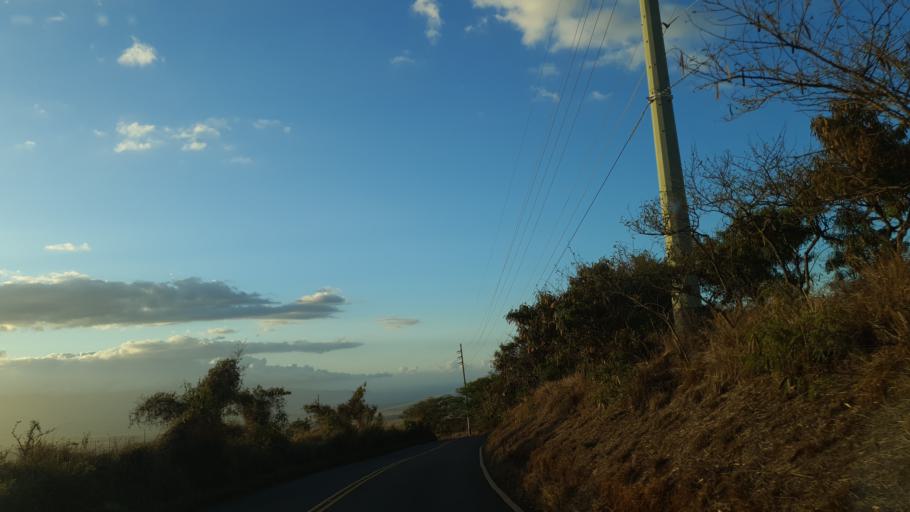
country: US
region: Hawaii
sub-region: Maui County
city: Pukalani
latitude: 20.7882
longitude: -156.3521
